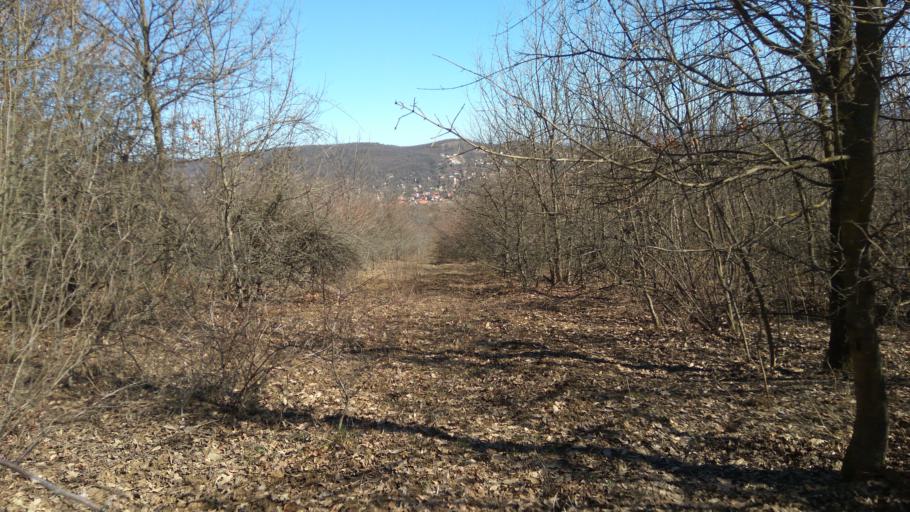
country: HU
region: Pest
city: Csobanka
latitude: 47.6430
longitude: 18.9869
